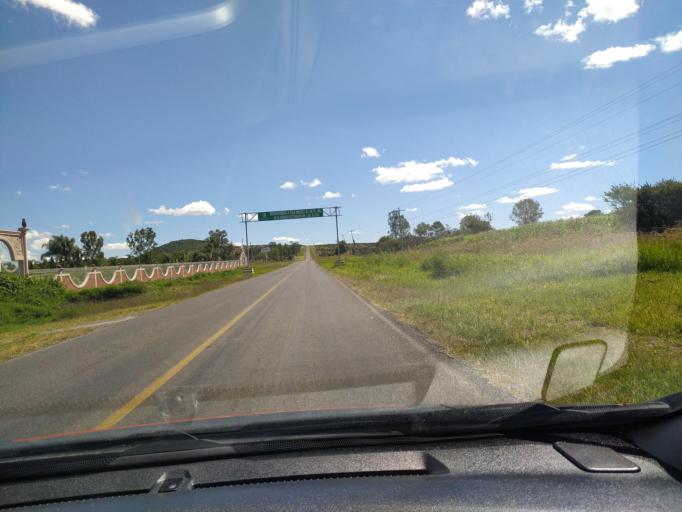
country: MX
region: Jalisco
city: San Miguel el Alto
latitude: 21.0206
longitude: -102.4511
